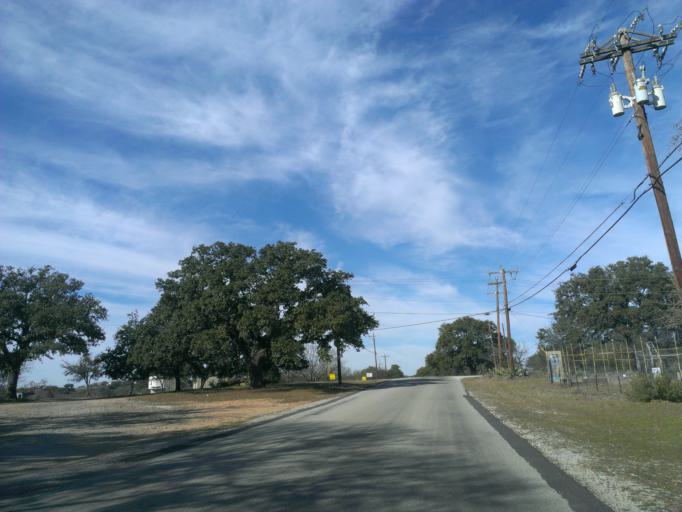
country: US
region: Texas
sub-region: Burnet County
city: Granite Shoals
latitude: 30.6029
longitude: -98.4119
